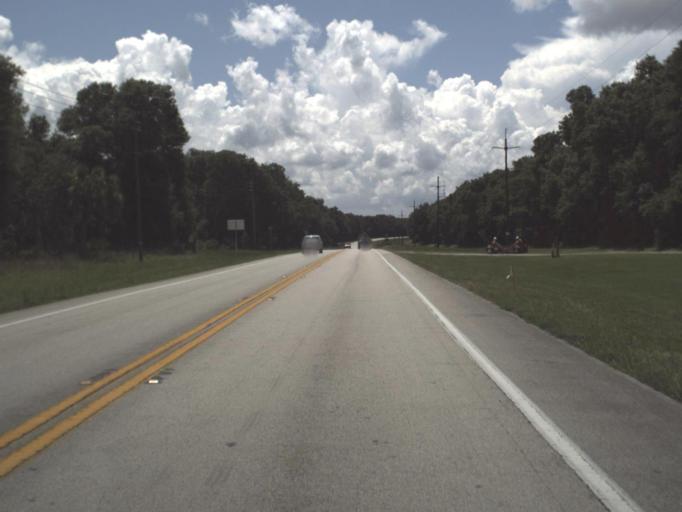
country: US
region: Florida
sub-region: Putnam County
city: Palatka
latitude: 29.5200
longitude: -81.6242
